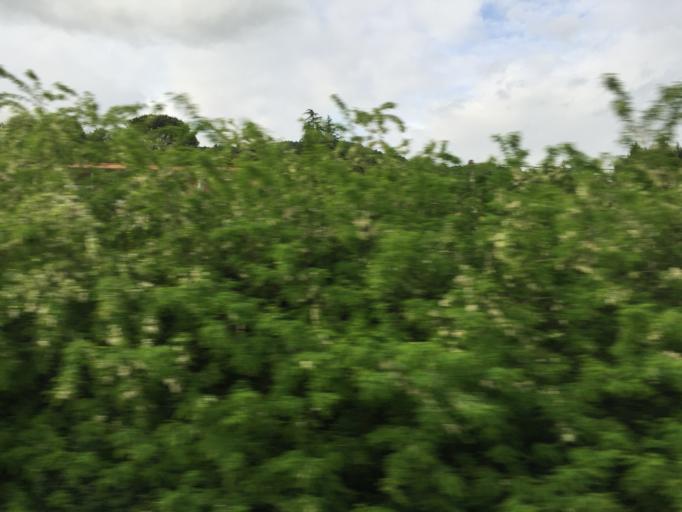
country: FR
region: Rhone-Alpes
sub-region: Departement de la Drome
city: Saint-Vallier
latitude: 45.1622
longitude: 4.8292
